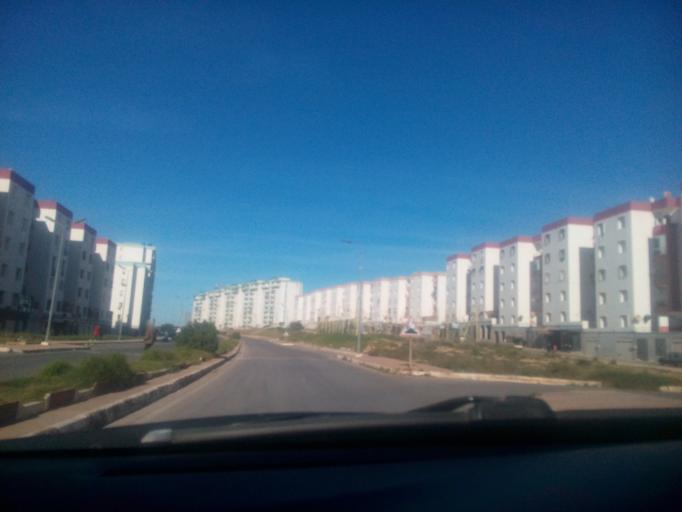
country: DZ
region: Oran
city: Bir el Djir
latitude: 35.7514
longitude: -0.5530
